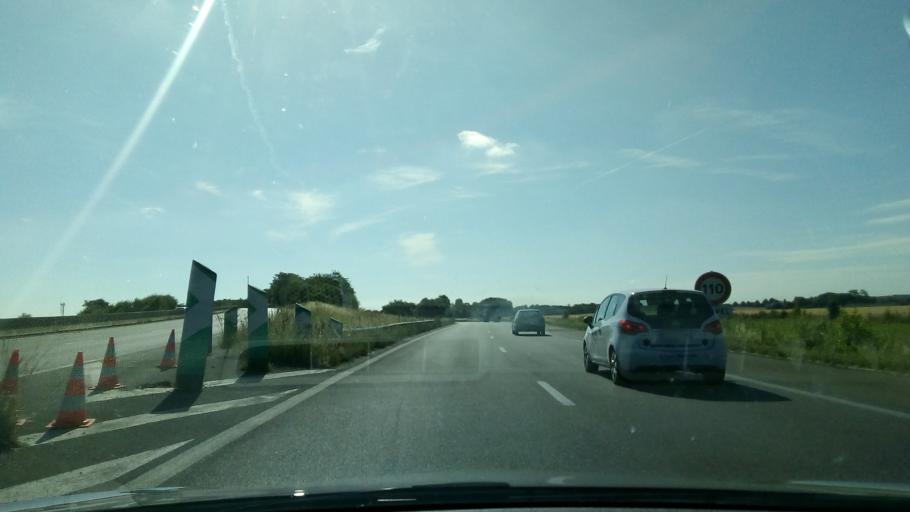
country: FR
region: Ile-de-France
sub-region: Departement de Seine-et-Marne
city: Vert-Saint-Denis
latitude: 48.5936
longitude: 2.6199
